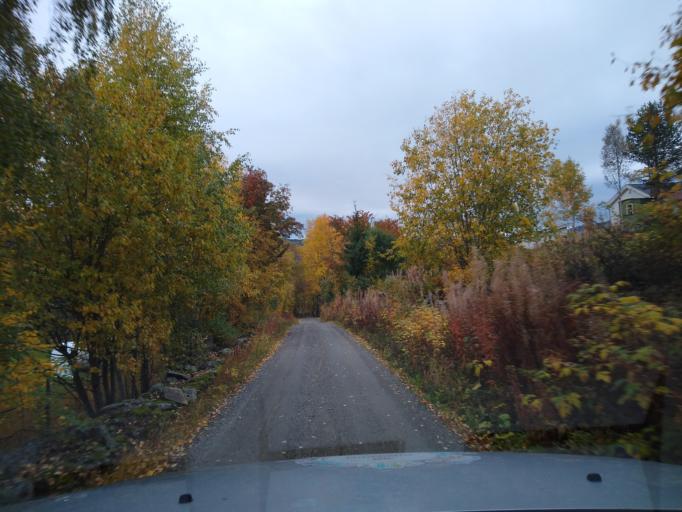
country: NO
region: Oppland
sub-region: Ringebu
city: Ringebu
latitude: 61.5438
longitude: 10.1261
